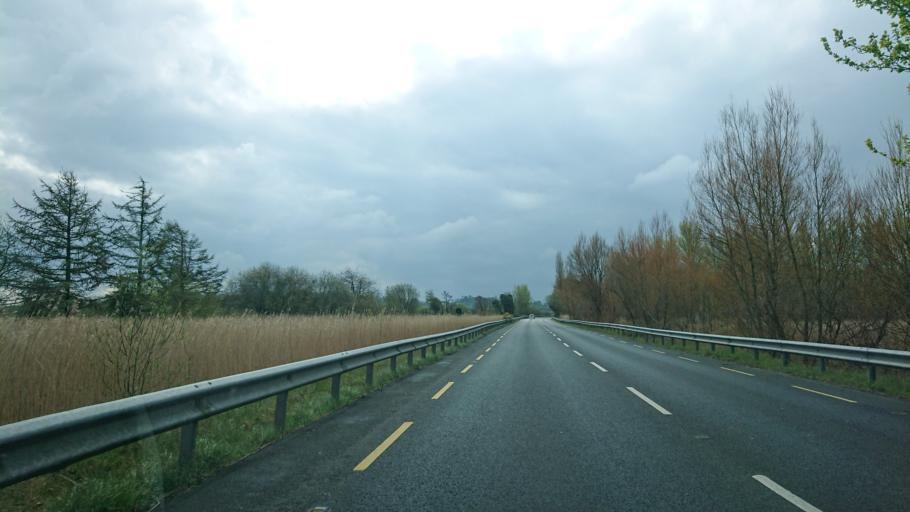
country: IE
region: Munster
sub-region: Waterford
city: Waterford
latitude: 52.2333
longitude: -7.1215
